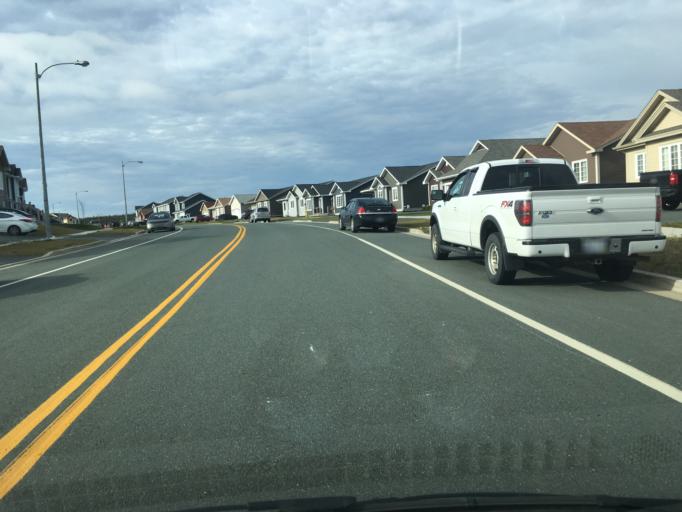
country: CA
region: Newfoundland and Labrador
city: Mount Pearl
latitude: 47.5560
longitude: -52.7996
